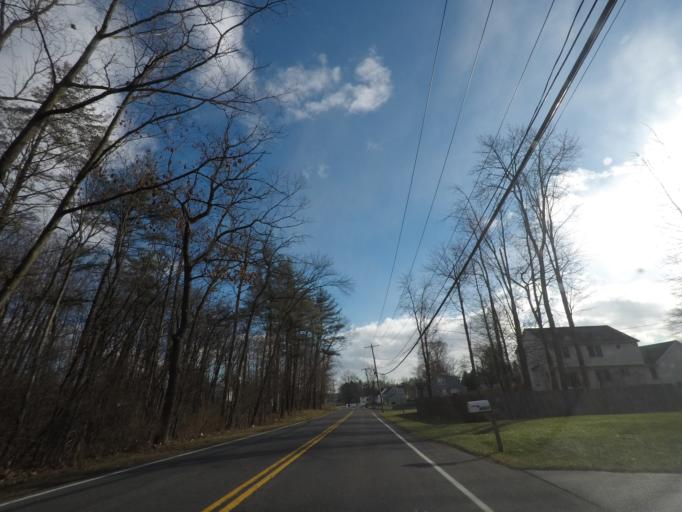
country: US
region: New York
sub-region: Schenectady County
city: Niskayuna
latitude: 42.7575
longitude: -73.8830
